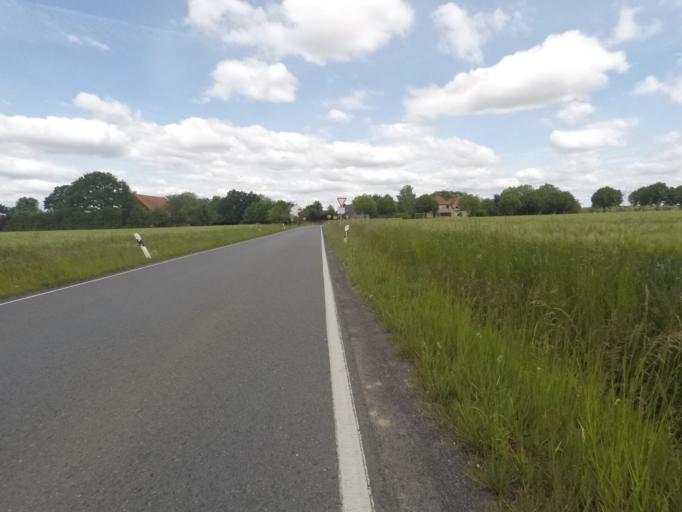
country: DE
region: North Rhine-Westphalia
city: Enger
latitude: 52.1859
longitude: 8.5305
